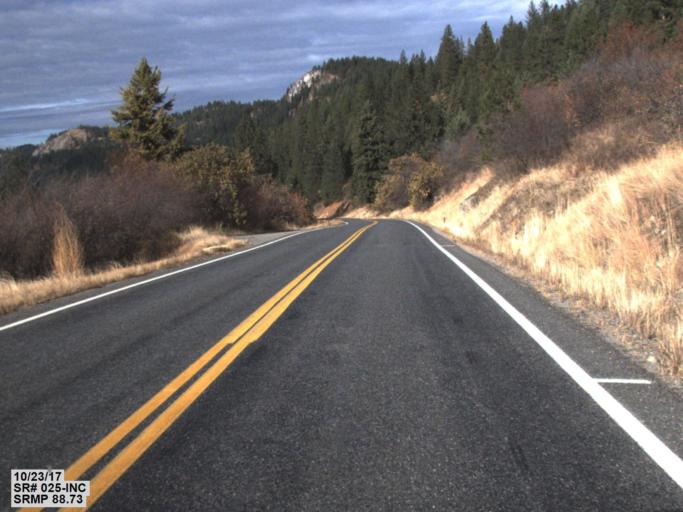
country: US
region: Washington
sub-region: Stevens County
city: Kettle Falls
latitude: 48.6809
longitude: -118.0151
